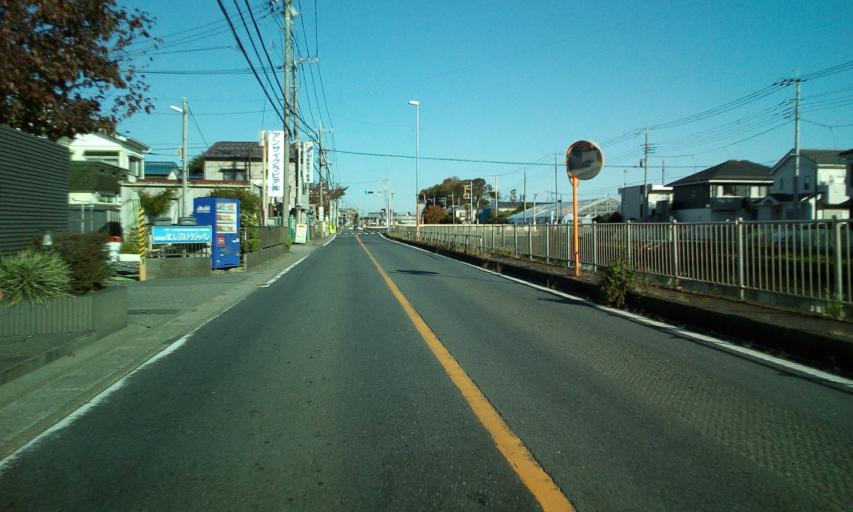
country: JP
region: Chiba
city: Nagareyama
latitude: 35.8234
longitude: 139.8831
